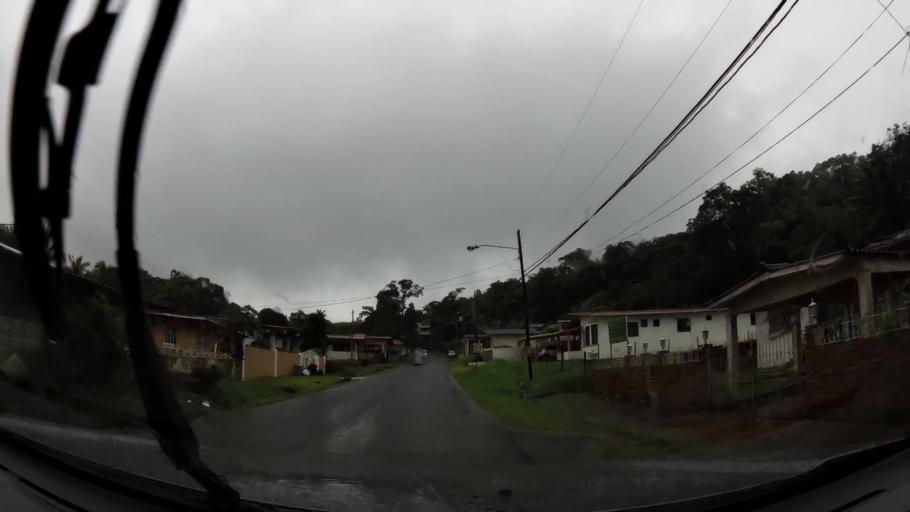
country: PA
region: Colon
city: Sabanitas
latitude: 9.3417
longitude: -79.8096
